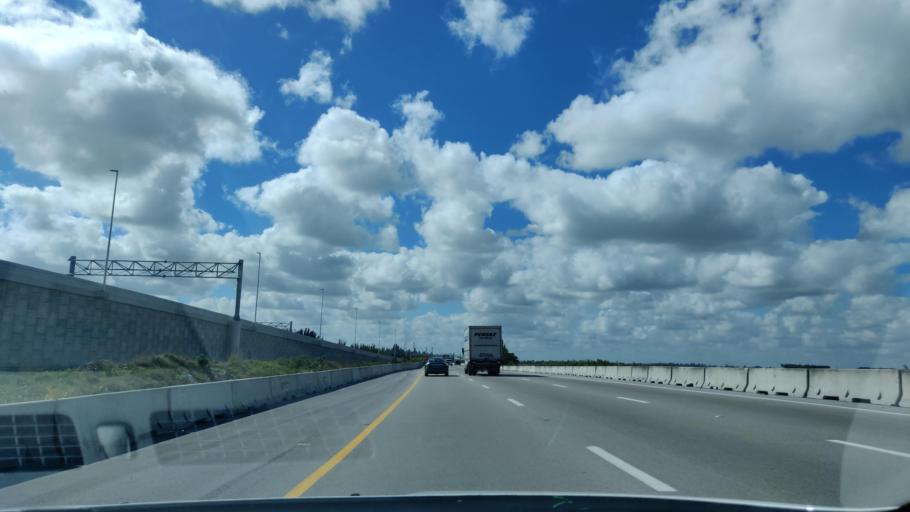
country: US
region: Florida
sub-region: Miami-Dade County
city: Palm Springs North
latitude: 25.9269
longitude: -80.3765
